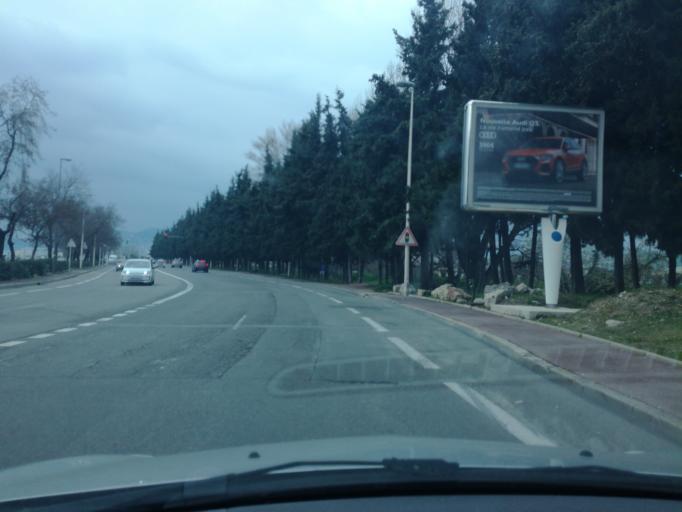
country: FR
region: Provence-Alpes-Cote d'Azur
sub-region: Departement des Alpes-Maritimes
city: Mandelieu-la-Napoule
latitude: 43.5538
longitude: 6.9638
